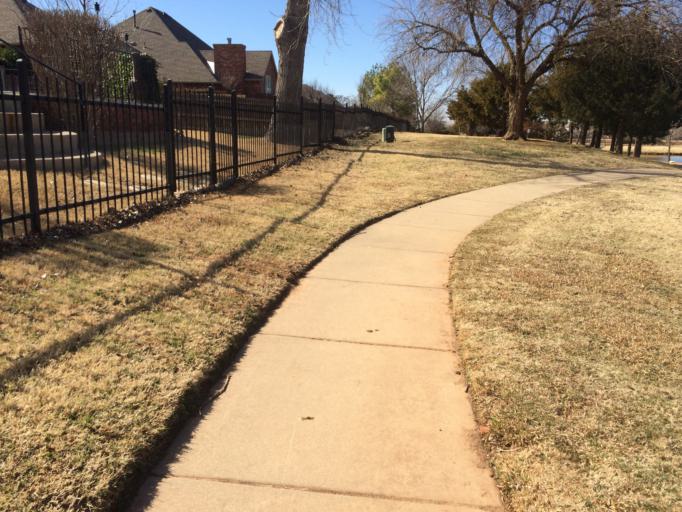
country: US
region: Oklahoma
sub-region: Cleveland County
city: Hall Park
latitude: 35.2140
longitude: -97.3984
